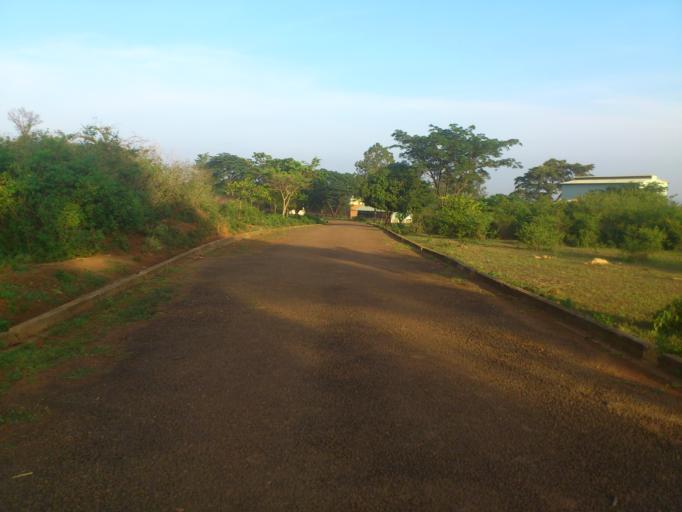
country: UG
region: Eastern Region
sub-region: Busia District
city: Busia
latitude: 0.5438
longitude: 34.0229
